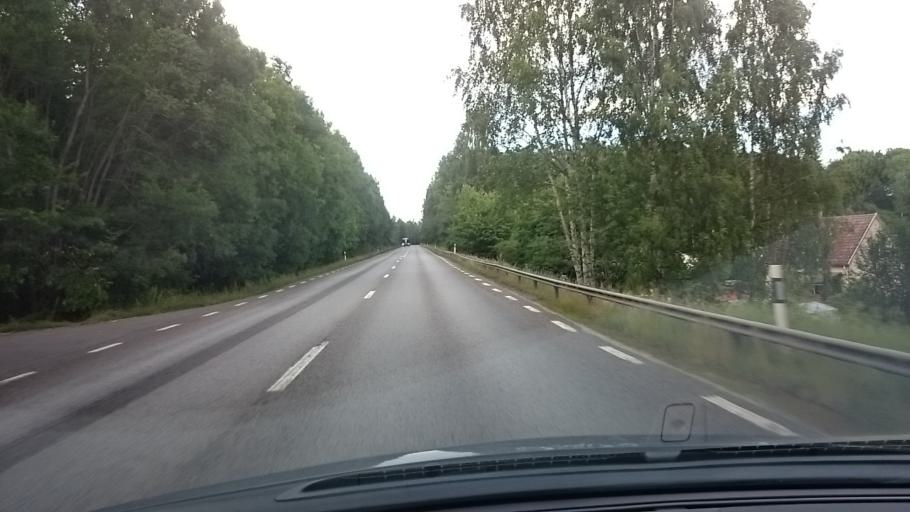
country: SE
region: OErebro
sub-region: Askersunds Kommun
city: Askersund
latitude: 58.7539
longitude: 14.7918
